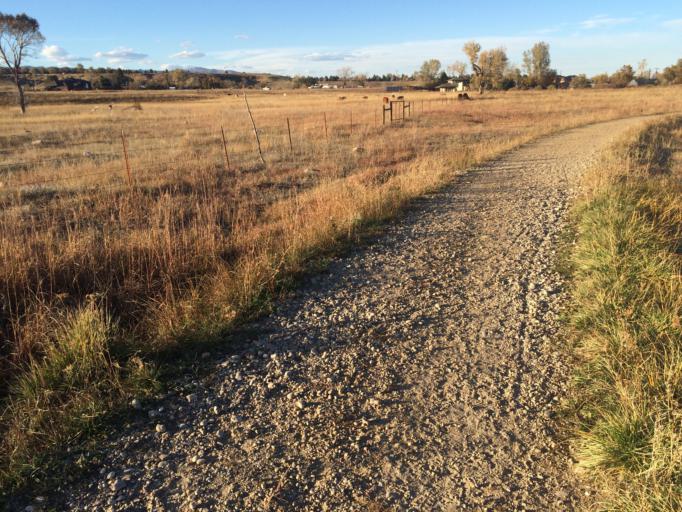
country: US
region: Colorado
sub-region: Boulder County
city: Boulder
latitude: 39.9577
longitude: -105.2396
